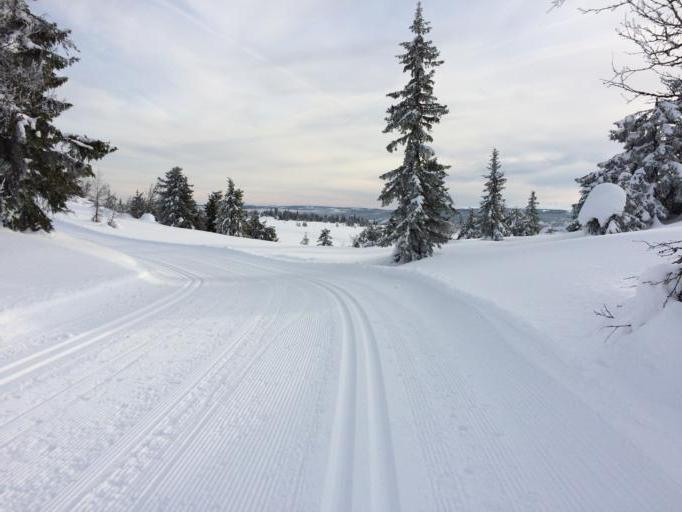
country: NO
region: Oppland
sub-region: Gausdal
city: Segalstad bru
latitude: 61.3281
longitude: 10.0340
